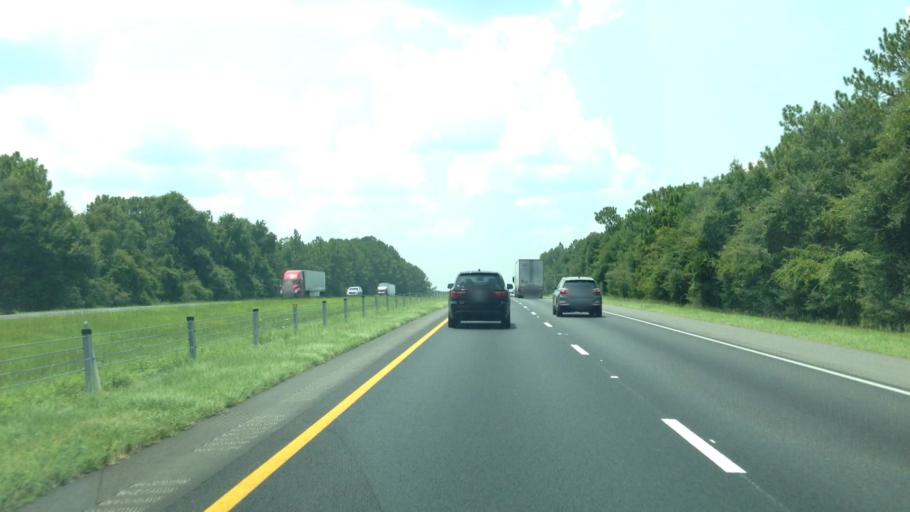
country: US
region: Florida
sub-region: Okaloosa County
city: Crestview
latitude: 30.7152
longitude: -86.6833
